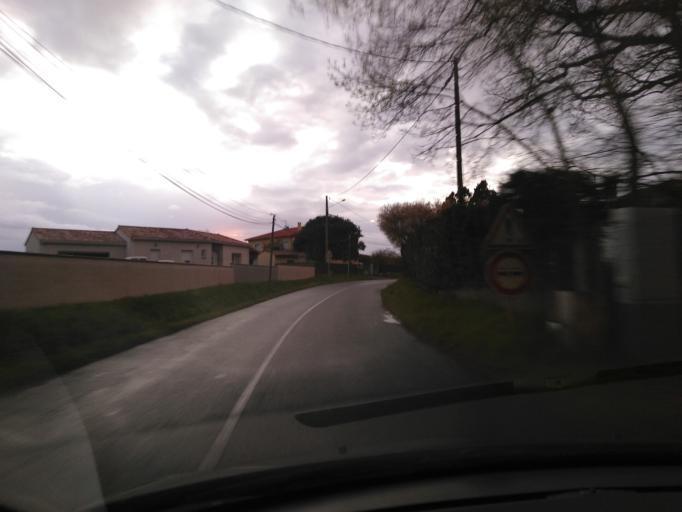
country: FR
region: Midi-Pyrenees
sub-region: Departement de la Haute-Garonne
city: Seilh
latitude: 43.6772
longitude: 1.3497
